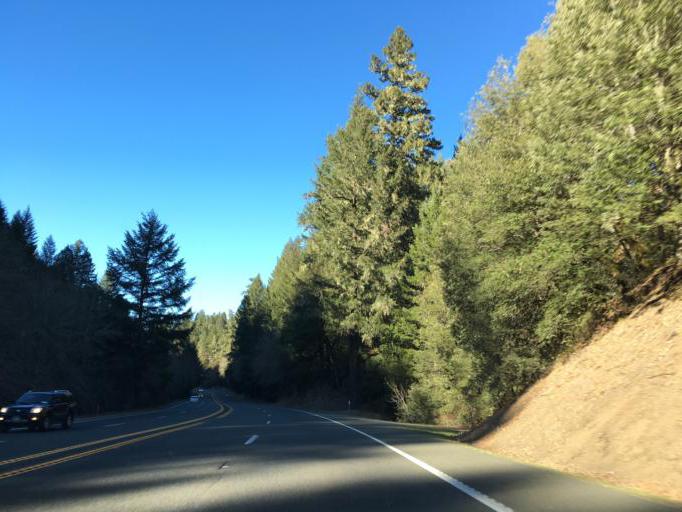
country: US
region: California
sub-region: Mendocino County
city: Laytonville
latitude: 39.5751
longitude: -123.4387
